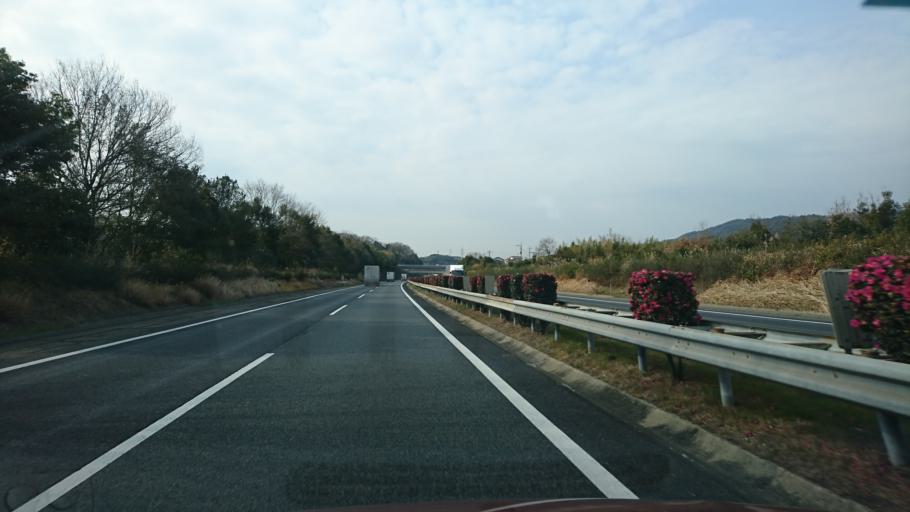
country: JP
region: Hiroshima
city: Kannabecho-yahiro
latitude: 34.5315
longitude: 133.4512
